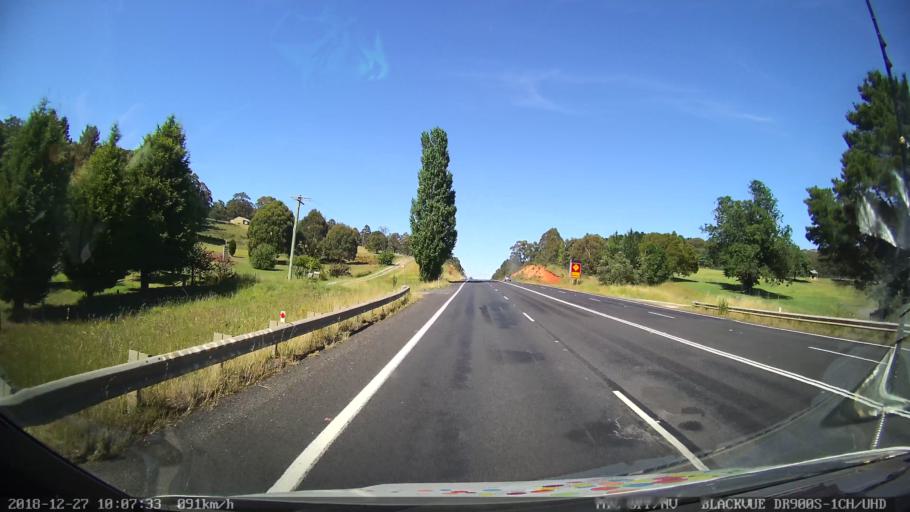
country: AU
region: New South Wales
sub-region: Lithgow
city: Portland
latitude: -33.4409
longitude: 149.8379
